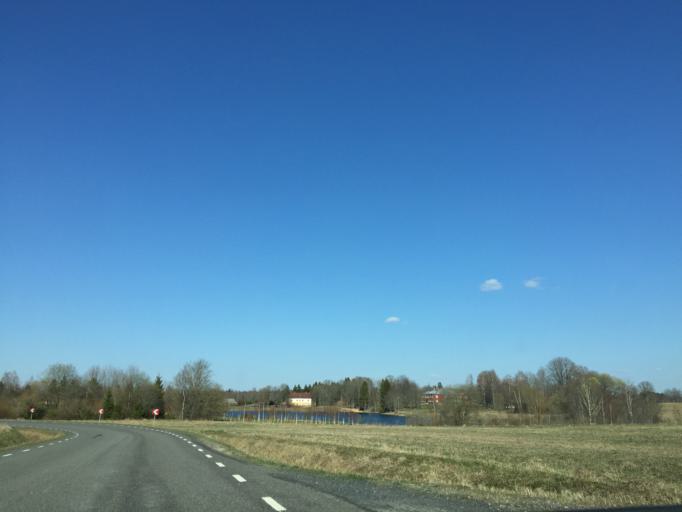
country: EE
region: Viljandimaa
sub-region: Viiratsi vald
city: Viiratsi
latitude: 58.2738
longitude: 25.6854
